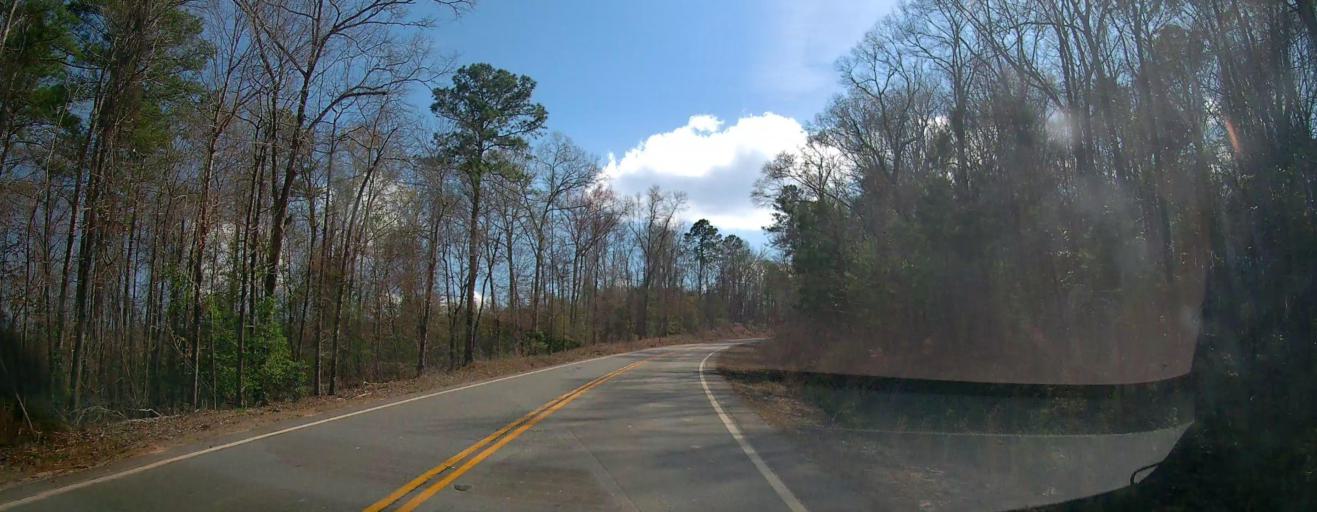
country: US
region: Georgia
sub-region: Wilkinson County
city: Gordon
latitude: 32.8114
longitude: -83.3238
